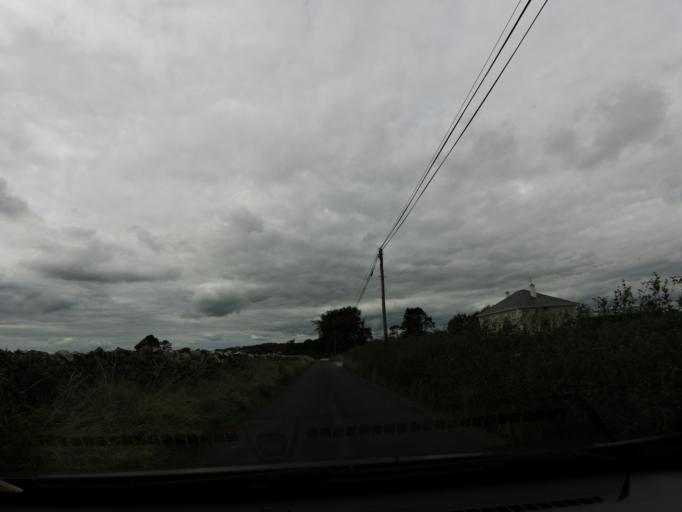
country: IE
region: Connaught
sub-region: County Galway
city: Loughrea
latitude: 53.1484
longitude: -8.4204
